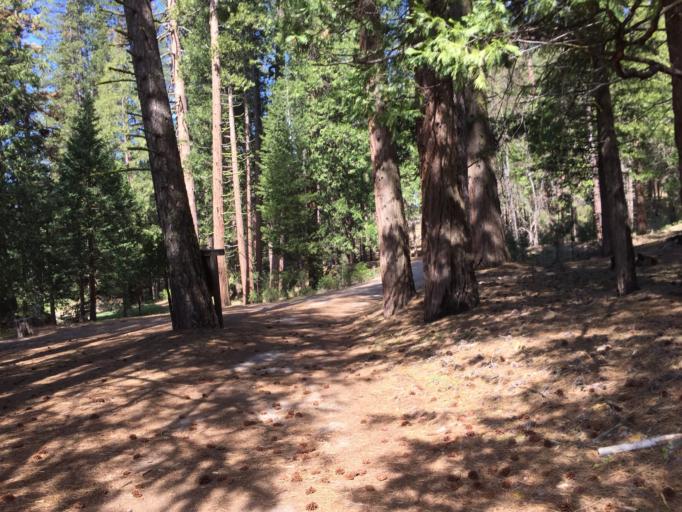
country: US
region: California
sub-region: Madera County
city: Ahwahnee
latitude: 37.5344
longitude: -119.6496
